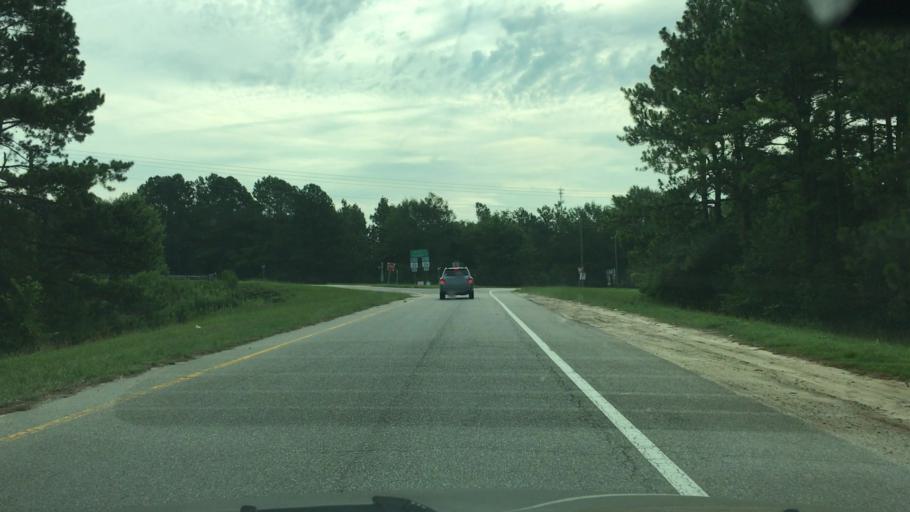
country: US
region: South Carolina
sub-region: Lexington County
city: Batesburg
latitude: 33.7507
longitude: -81.5273
